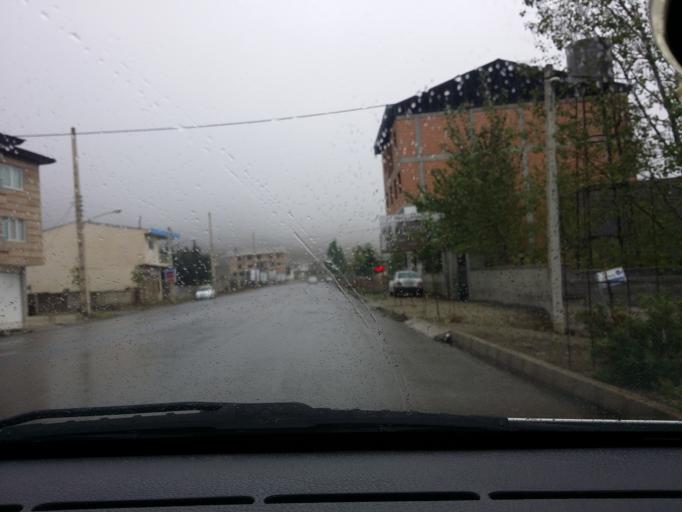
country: IR
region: Mazandaran
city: Chalus
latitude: 36.5220
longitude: 51.2349
